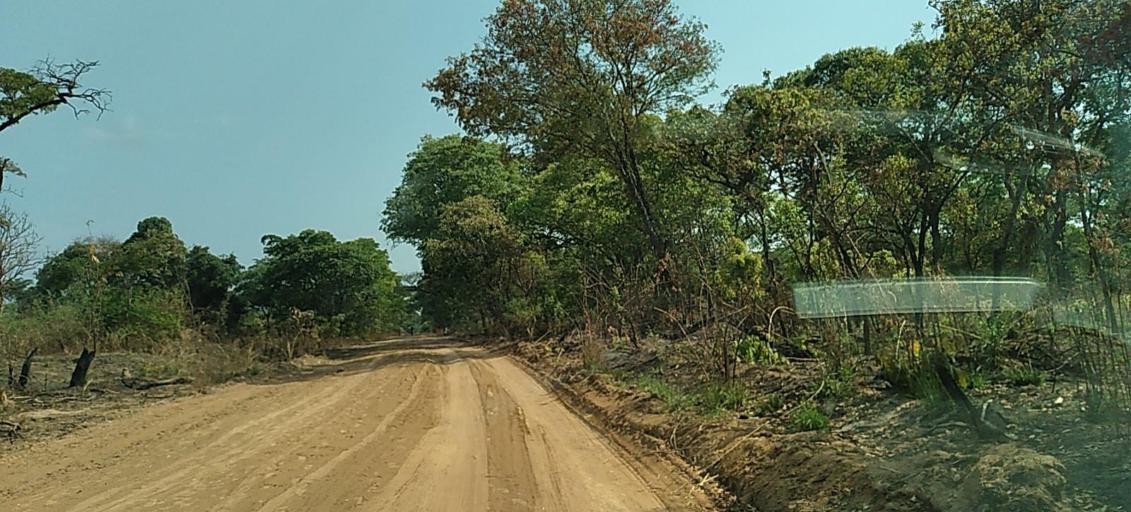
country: ZM
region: Copperbelt
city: Kalulushi
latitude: -12.9122
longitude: 27.8232
